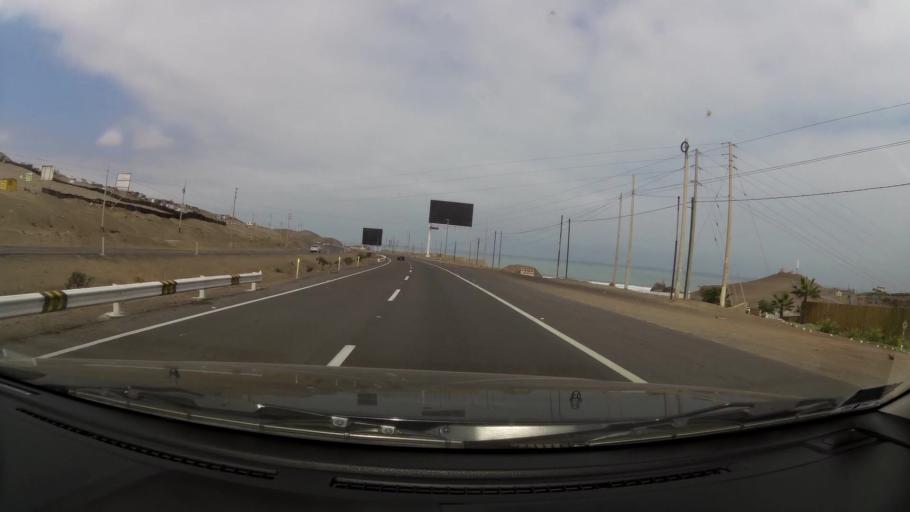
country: PE
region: Lima
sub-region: Provincia de Canete
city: Mala
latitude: -12.6203
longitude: -76.6702
